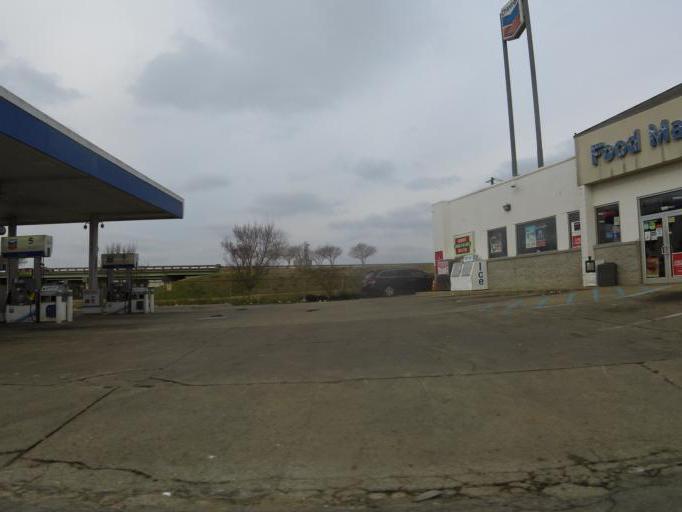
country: US
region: Alabama
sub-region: Montgomery County
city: Montgomery
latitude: 32.4036
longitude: -86.3079
